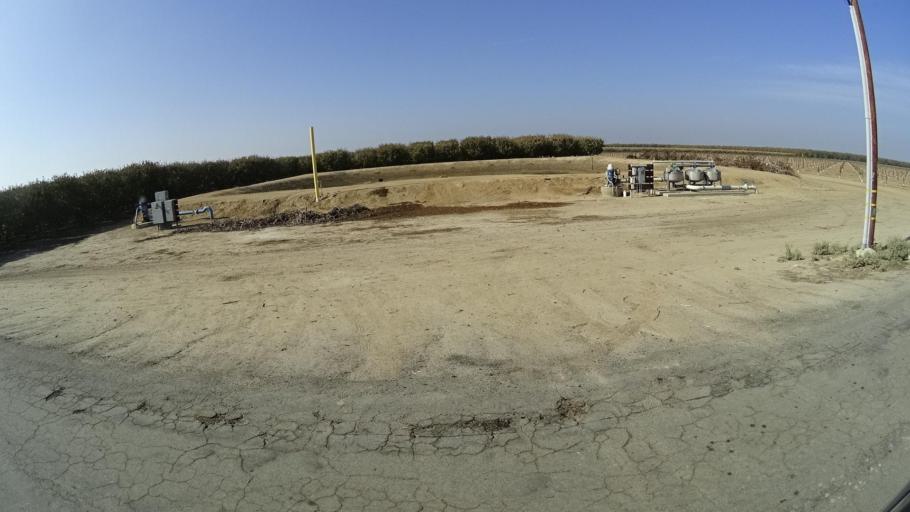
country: US
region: California
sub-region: Kern County
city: McFarland
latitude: 35.6199
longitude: -119.1864
